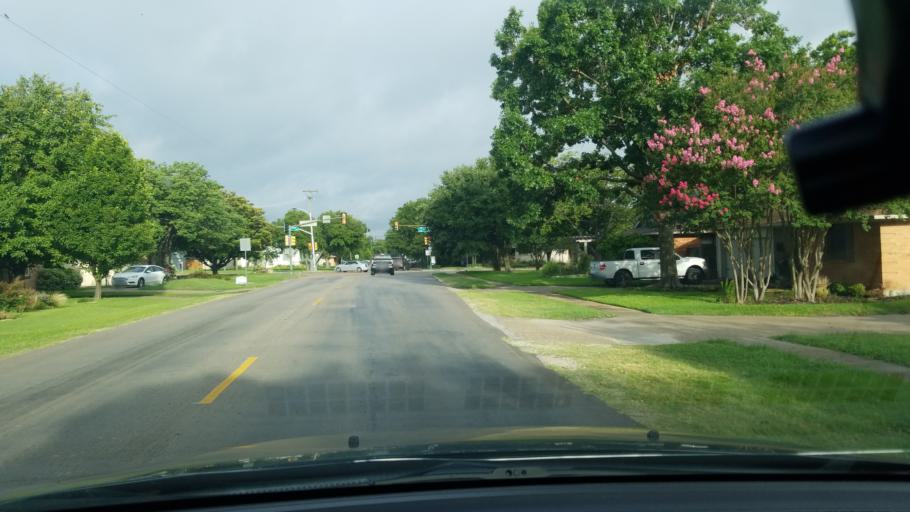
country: US
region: Texas
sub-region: Dallas County
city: Mesquite
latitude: 32.8218
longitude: -96.6833
